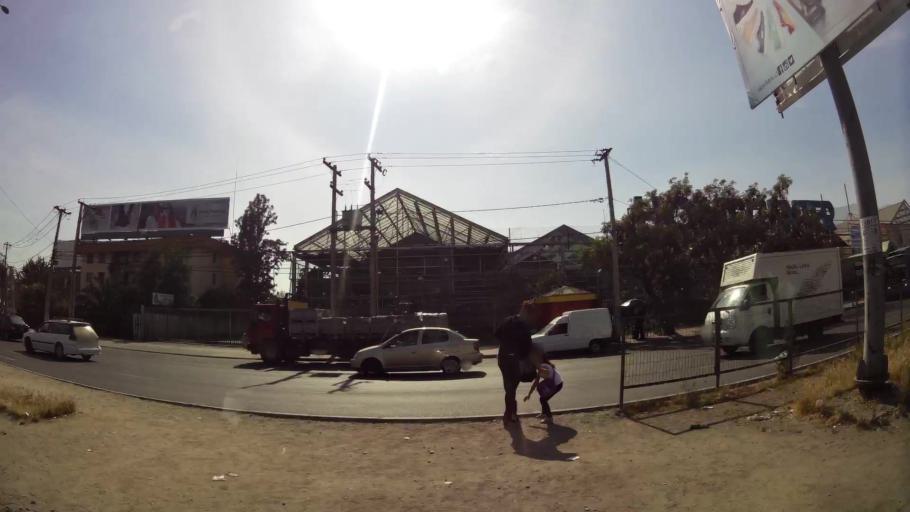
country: CL
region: Santiago Metropolitan
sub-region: Provincia de Santiago
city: Villa Presidente Frei, Nunoa, Santiago, Chile
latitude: -33.5089
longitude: -70.5892
